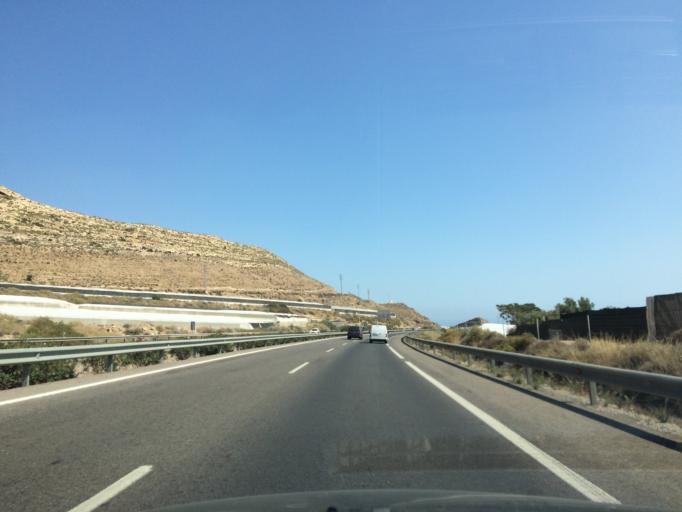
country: ES
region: Andalusia
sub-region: Provincia de Almeria
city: Vicar
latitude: 36.8136
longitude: -2.6433
